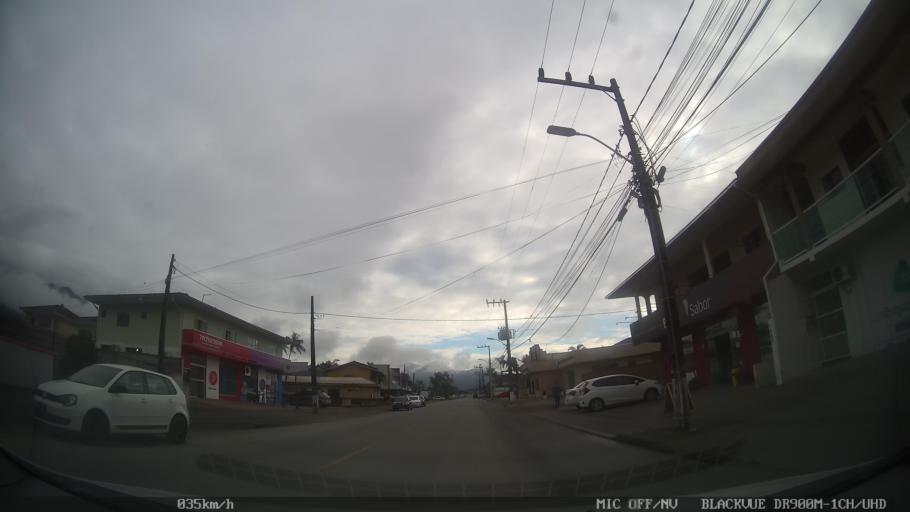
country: BR
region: Santa Catarina
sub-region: Joinville
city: Joinville
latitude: -26.0371
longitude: -48.8566
